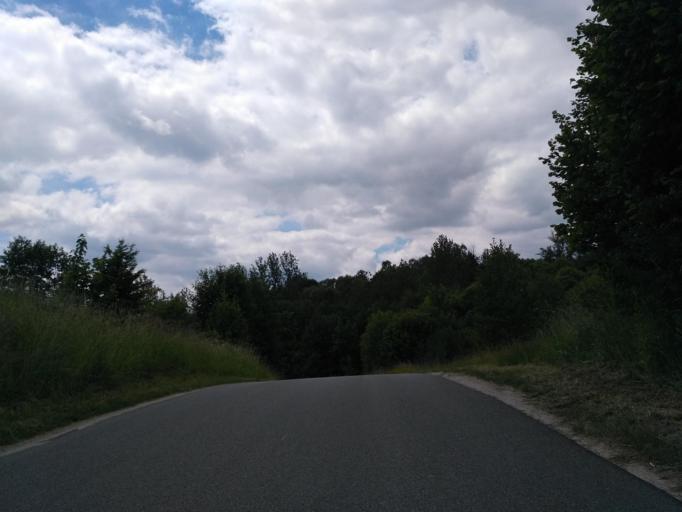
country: PL
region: Subcarpathian Voivodeship
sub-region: Powiat przeworski
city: Jawornik Polski
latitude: 49.8455
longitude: 22.3019
